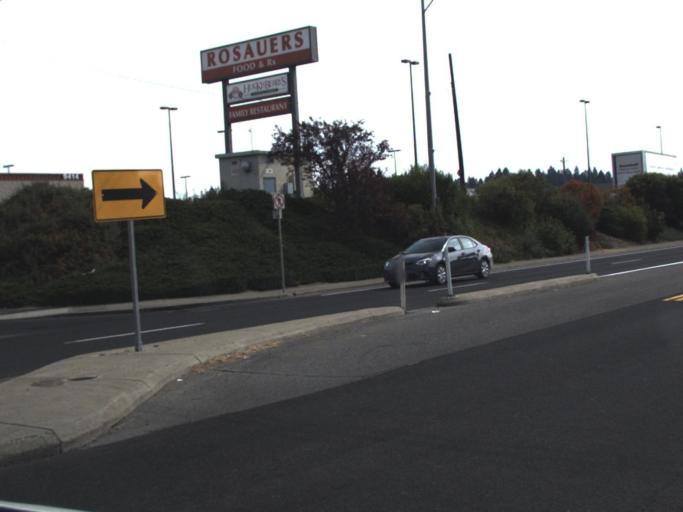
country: US
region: Washington
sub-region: Spokane County
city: Country Homes
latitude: 47.7439
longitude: -117.4116
